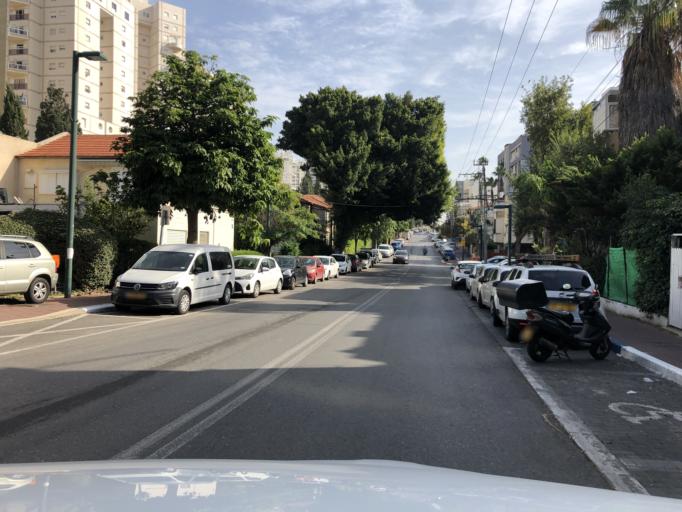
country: IL
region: Tel Aviv
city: Bene Beraq
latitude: 32.0701
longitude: 34.8291
